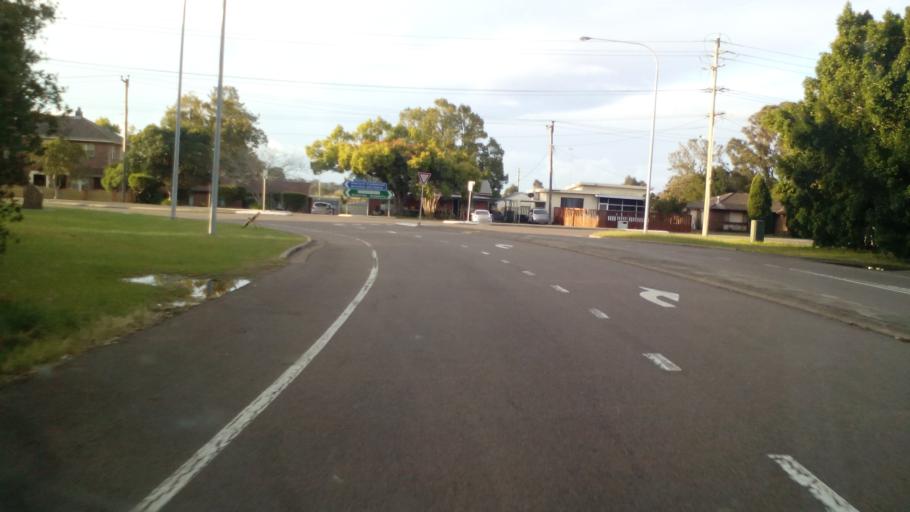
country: AU
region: New South Wales
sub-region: Newcastle
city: Beresfield
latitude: -32.8105
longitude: 151.6662
